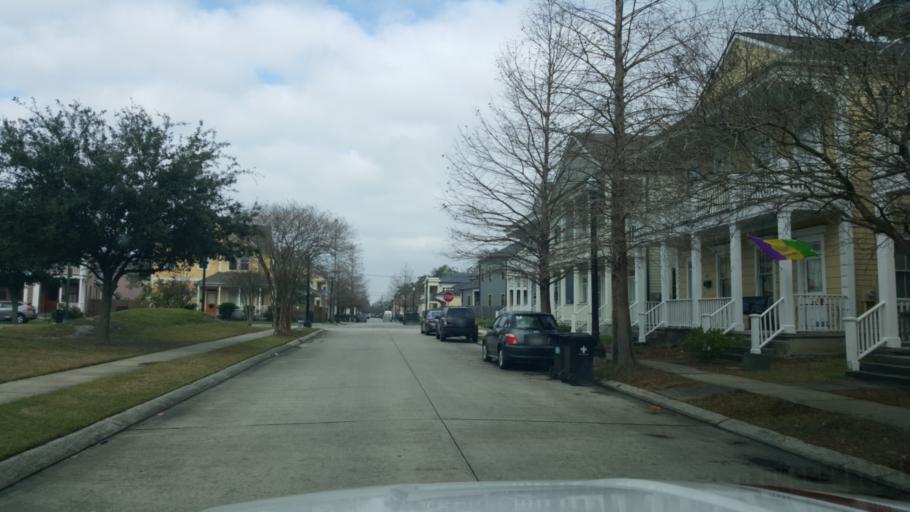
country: US
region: Louisiana
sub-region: Jefferson Parish
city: Gretna
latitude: 29.9281
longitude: -90.0703
